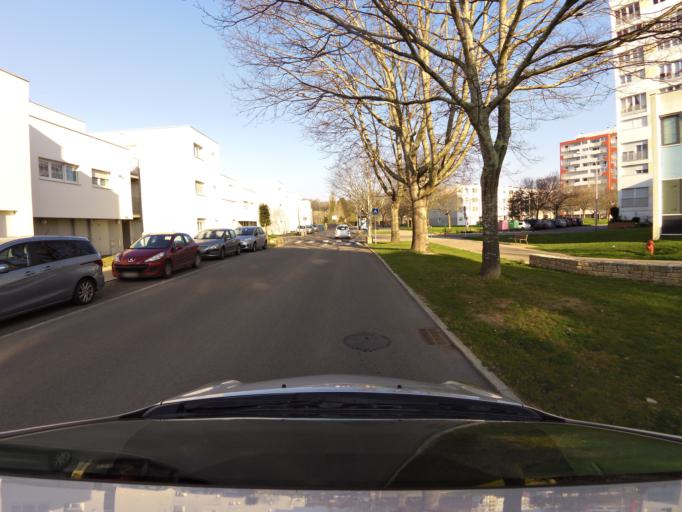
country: FR
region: Brittany
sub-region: Departement du Morbihan
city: Lorient
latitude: 47.7396
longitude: -3.3943
